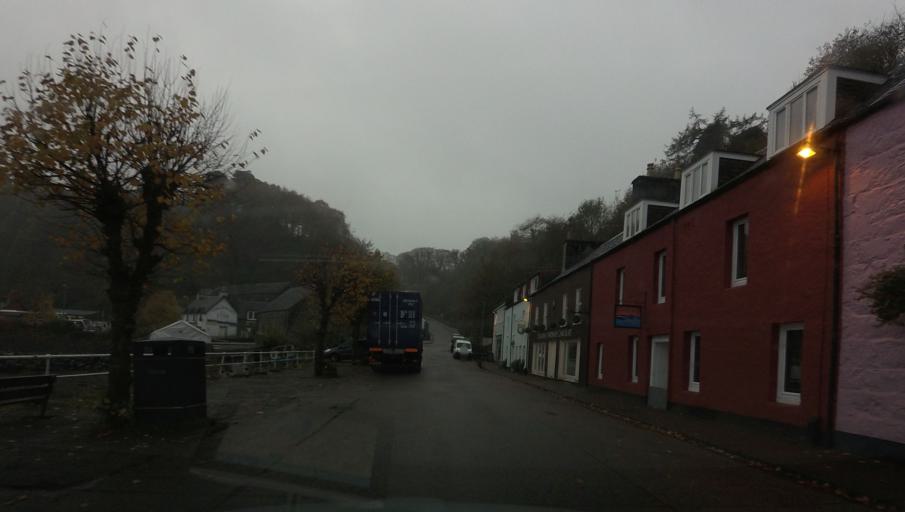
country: GB
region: Scotland
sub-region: Argyll and Bute
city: Isle Of Mull
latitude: 56.6217
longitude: -6.0696
